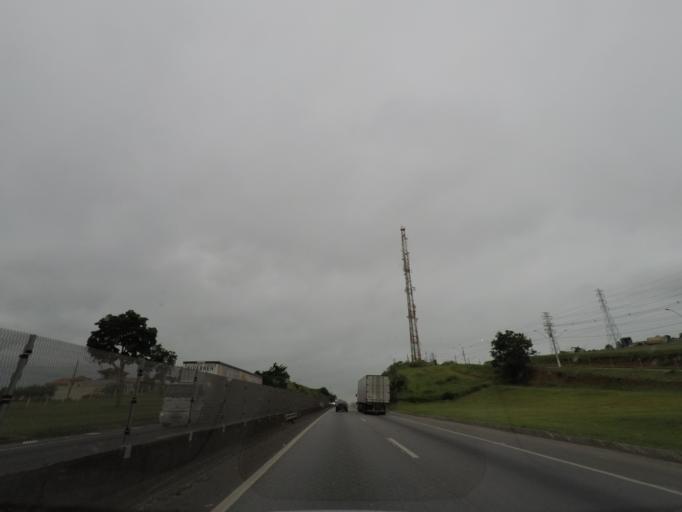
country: BR
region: Sao Paulo
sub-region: Taubate
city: Taubate
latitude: -23.0105
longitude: -45.5199
